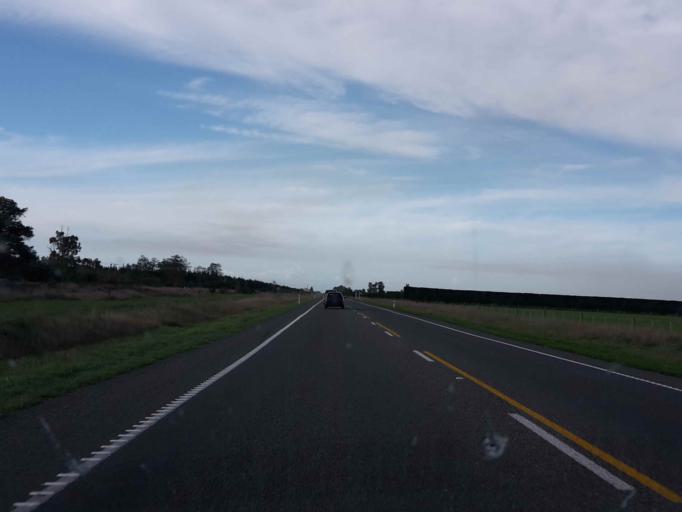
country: NZ
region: Canterbury
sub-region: Ashburton District
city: Tinwald
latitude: -43.9804
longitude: 171.6090
